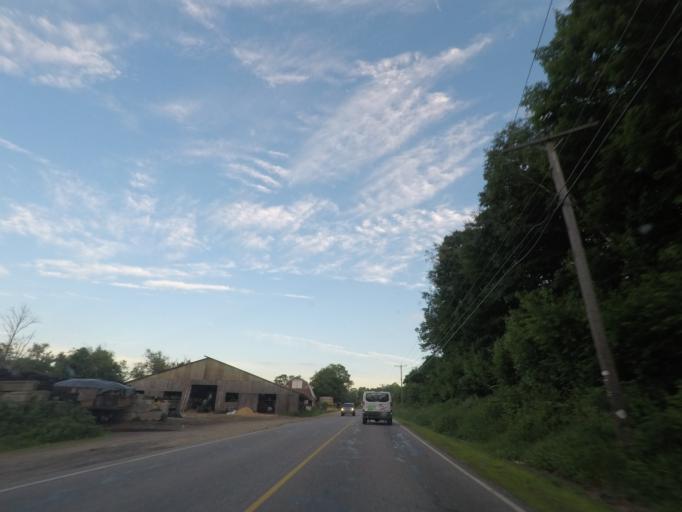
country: US
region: Massachusetts
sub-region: Worcester County
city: Fiskdale
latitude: 42.1660
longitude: -72.1477
